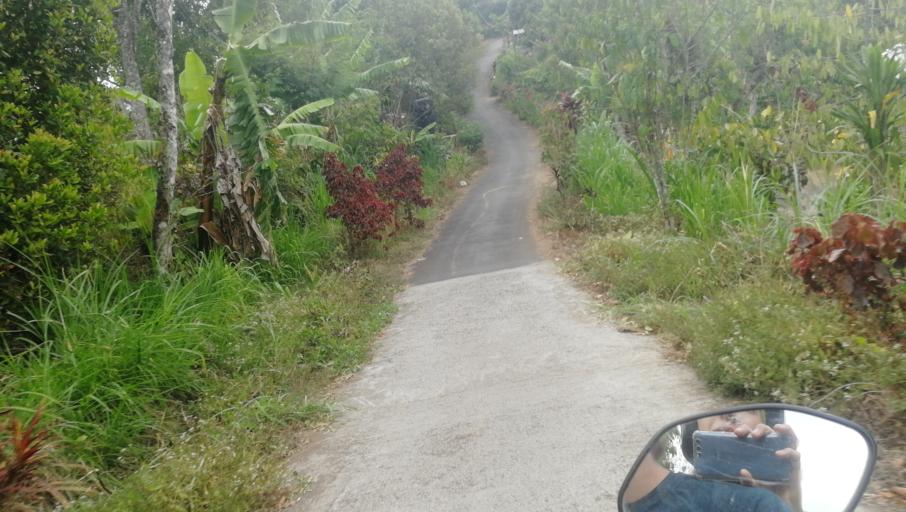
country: ID
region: Bali
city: Banjar Ambengan
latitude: -8.2093
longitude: 115.1104
